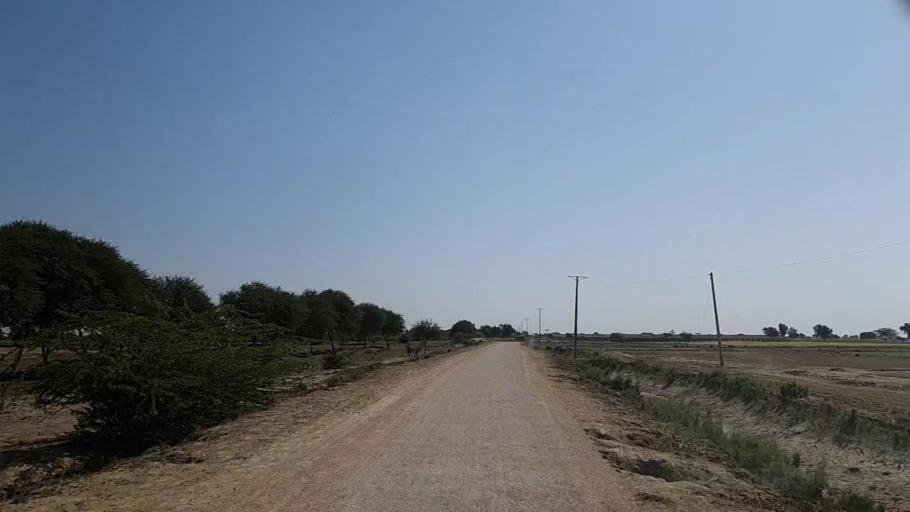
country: PK
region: Sindh
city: Mirpur Batoro
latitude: 24.6800
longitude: 68.2973
